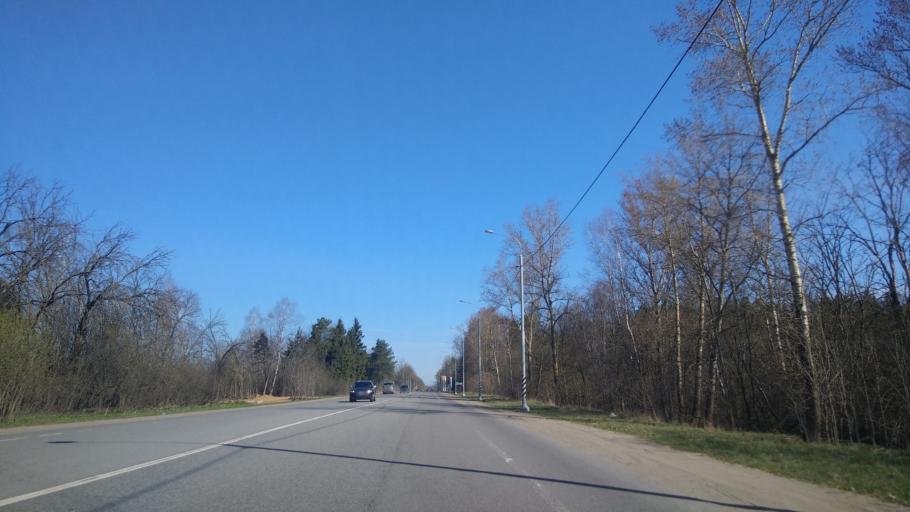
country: RU
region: Moskovskaya
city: Pushkino
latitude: 56.0270
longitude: 37.8711
